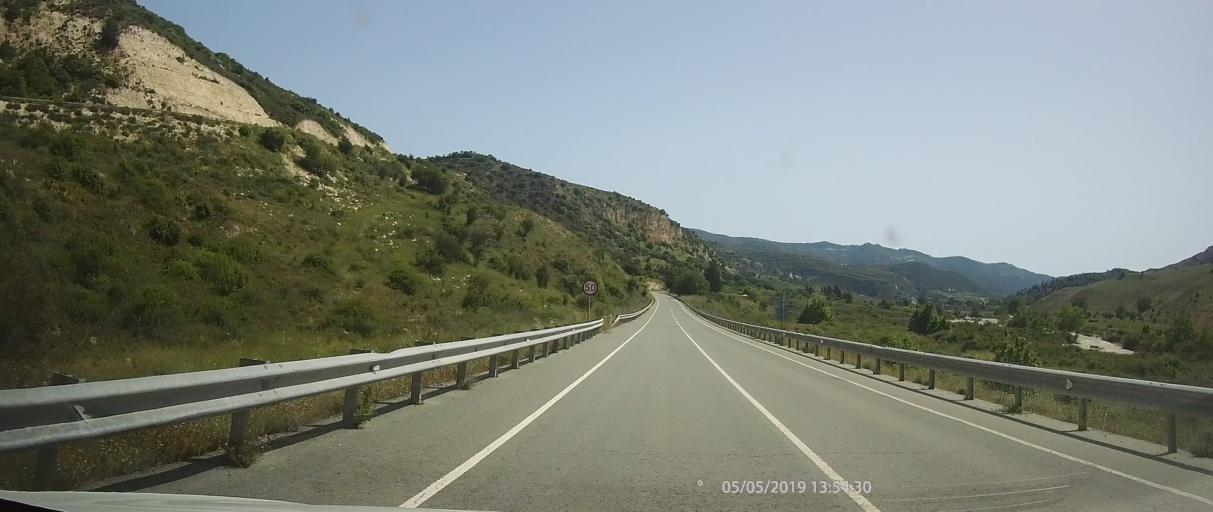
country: CY
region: Limassol
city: Pachna
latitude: 34.8206
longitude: 32.7203
